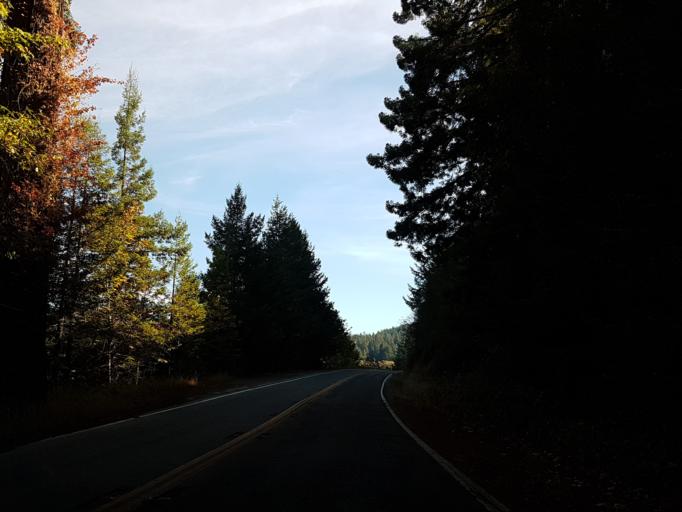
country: US
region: California
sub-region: Humboldt County
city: Rio Dell
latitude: 40.4271
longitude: -123.9819
